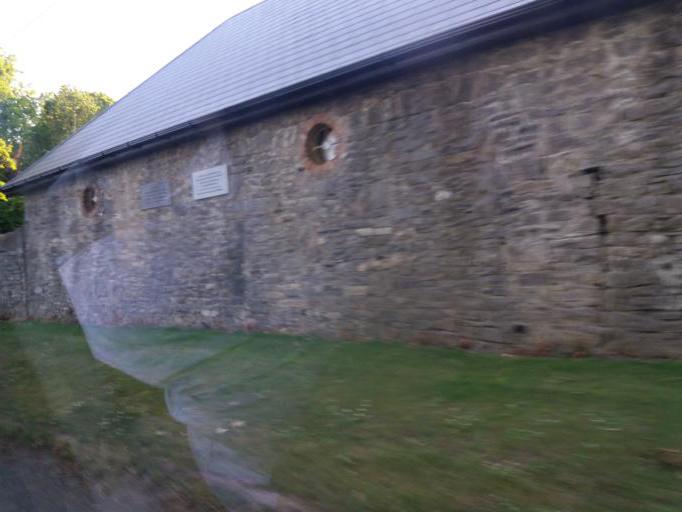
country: IE
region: Leinster
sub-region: An Mhi
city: Ashbourne
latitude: 53.5626
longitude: -6.3553
